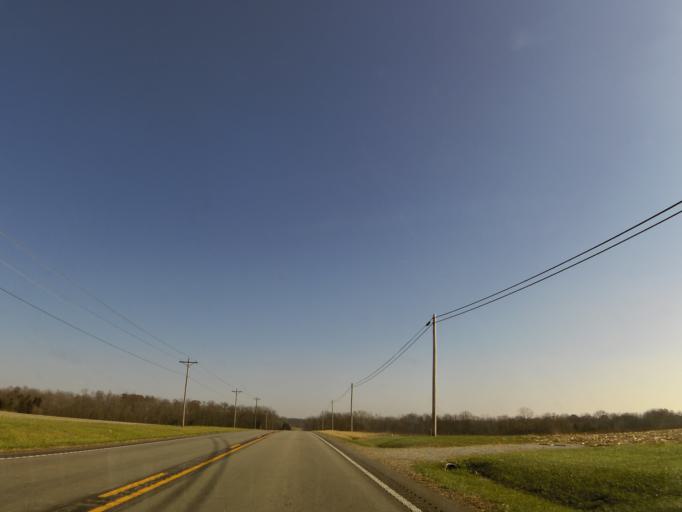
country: US
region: Indiana
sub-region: Union County
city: Liberty
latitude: 39.6401
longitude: -84.9610
